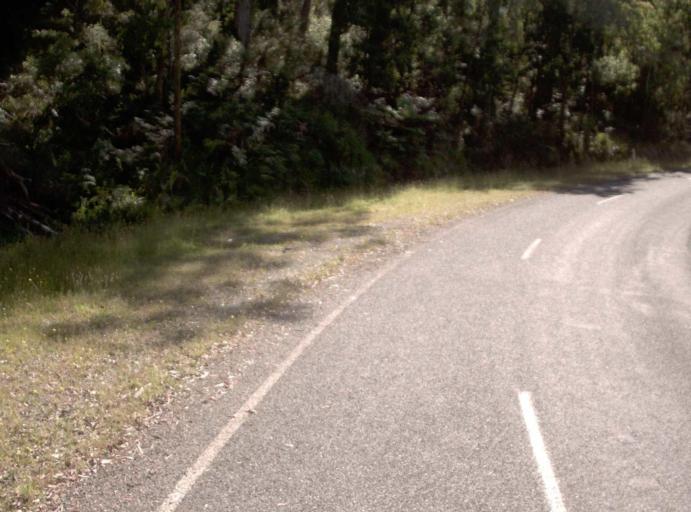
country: AU
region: New South Wales
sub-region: Bombala
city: Bombala
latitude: -37.3433
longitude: 148.6970
